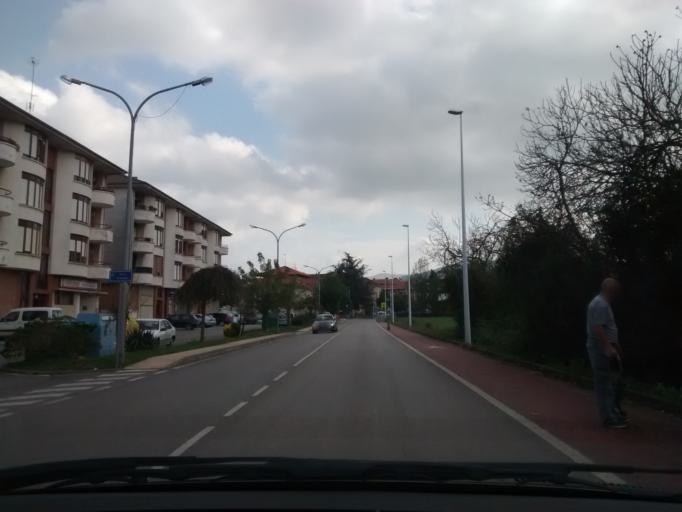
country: ES
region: Cantabria
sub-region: Provincia de Cantabria
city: Entrambasaguas
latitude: 43.3799
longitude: -3.6851
